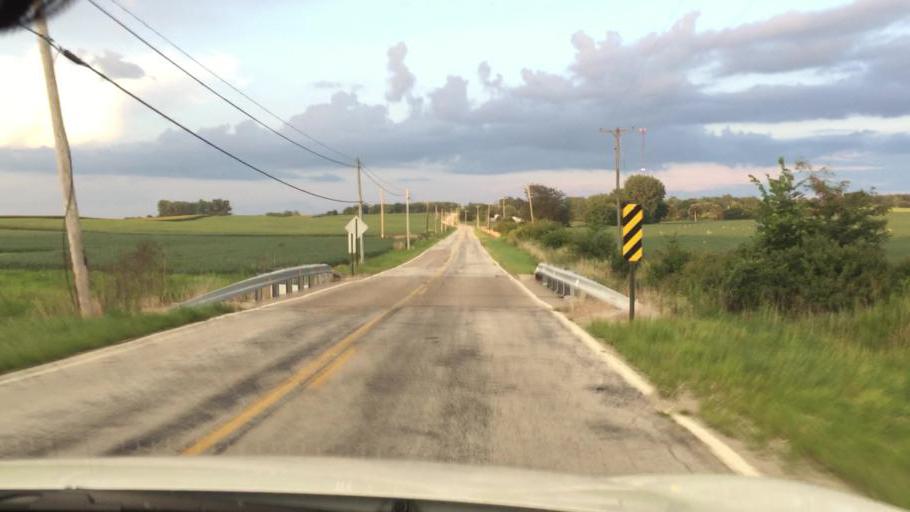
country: US
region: Ohio
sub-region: Champaign County
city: Mechanicsburg
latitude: 40.0070
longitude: -83.6070
